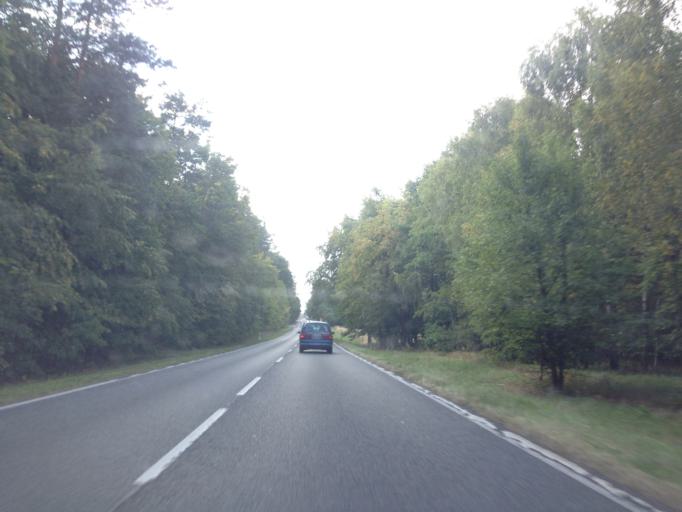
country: PL
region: Kujawsko-Pomorskie
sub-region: Powiat swiecki
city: Lniano
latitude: 53.4728
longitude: 18.1580
